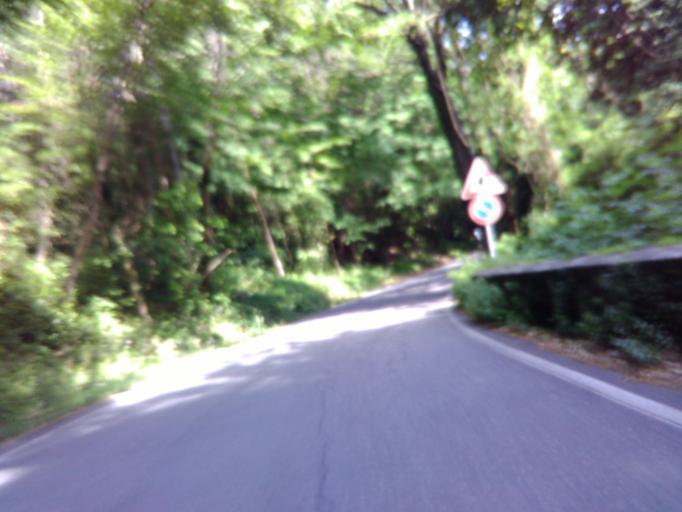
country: IT
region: Tuscany
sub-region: Provincia di Massa-Carrara
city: Fosdinovo
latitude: 44.1403
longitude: 10.0223
